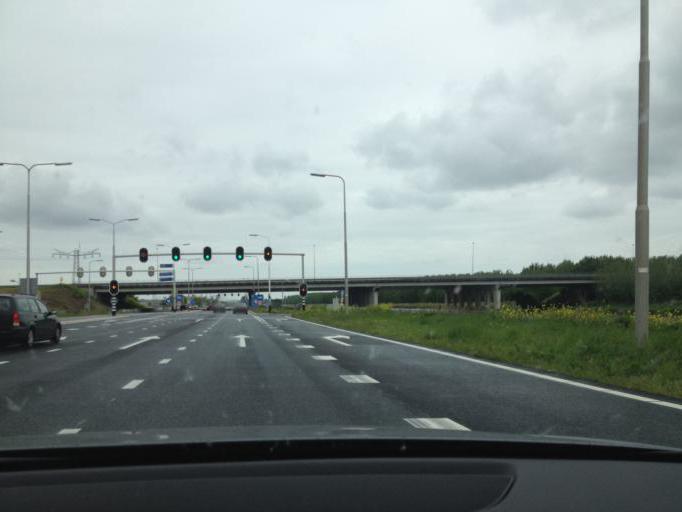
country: NL
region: Utrecht
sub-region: Gemeente Bunschoten
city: Spakenburg
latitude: 52.3135
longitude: 5.3348
